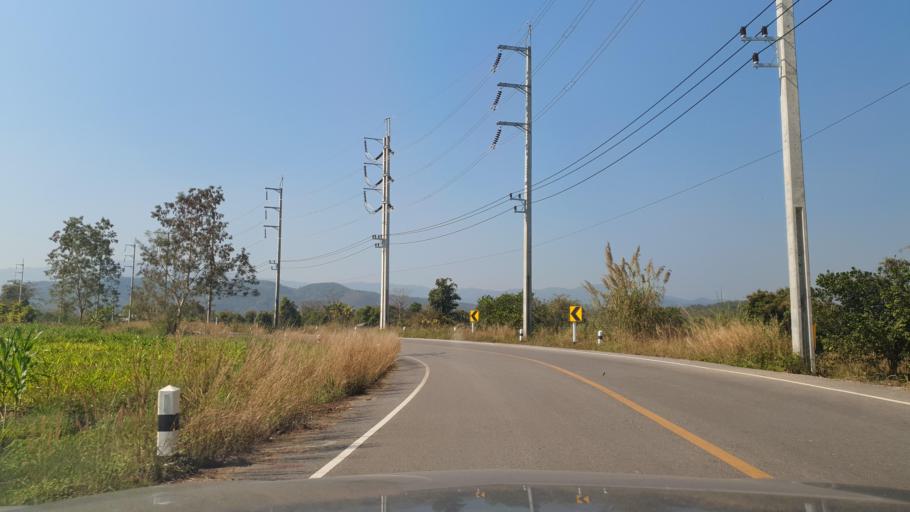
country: TH
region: Chiang Rai
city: Mae Lao
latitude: 19.8017
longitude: 99.6957
